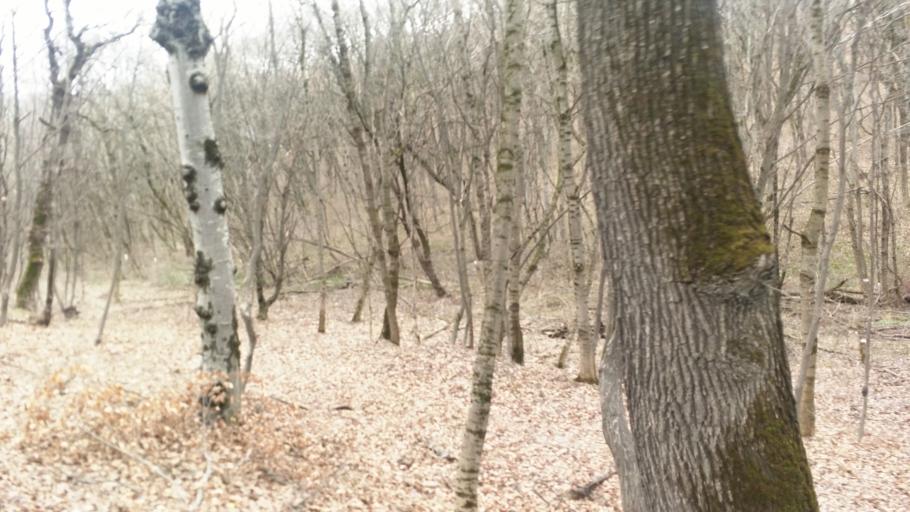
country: RU
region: Stavropol'skiy
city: Zheleznovodsk
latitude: 44.1370
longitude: 43.0163
